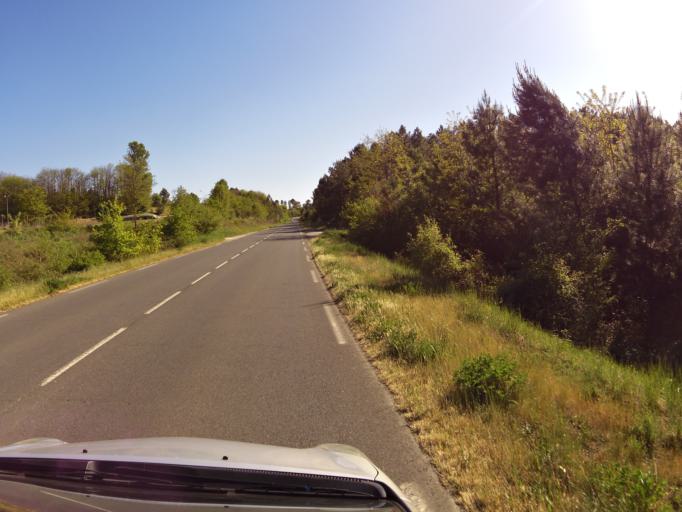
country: FR
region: Aquitaine
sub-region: Departement de la Dordogne
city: Sarlat-la-Caneda
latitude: 44.9644
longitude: 1.2373
